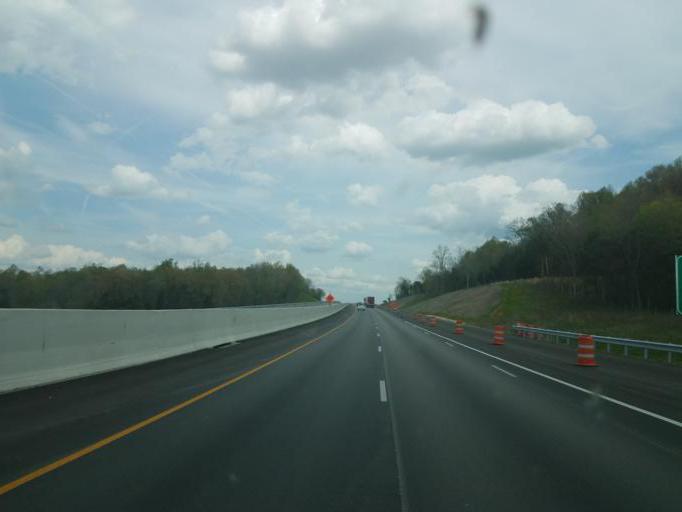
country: US
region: Kentucky
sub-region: Hart County
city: Munfordville
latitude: 37.3652
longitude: -85.8933
